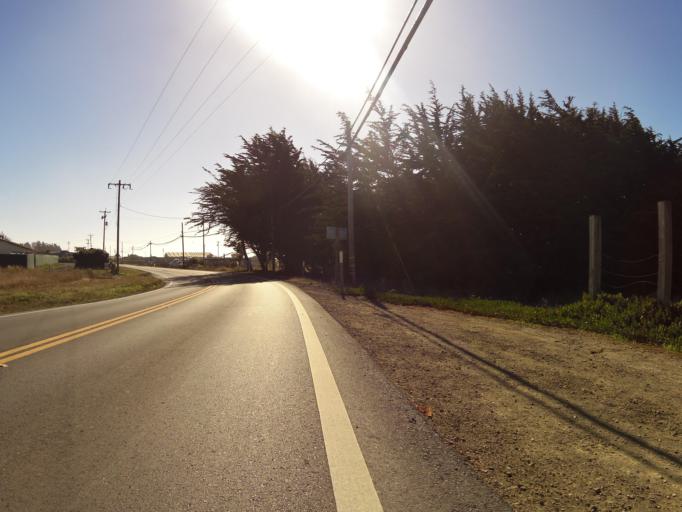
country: US
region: California
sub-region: Mendocino County
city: Fort Bragg
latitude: 39.4687
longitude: -123.8028
